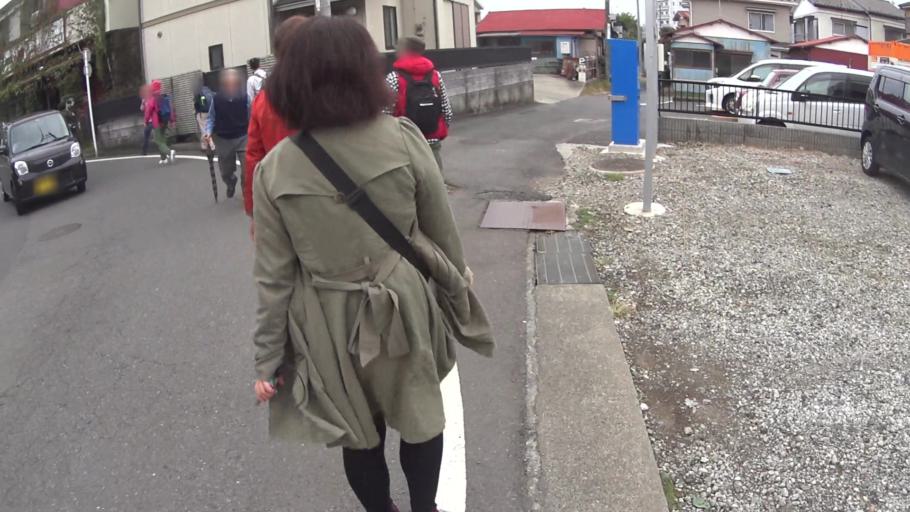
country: JP
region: Kanagawa
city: Hadano
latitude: 35.3777
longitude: 139.2262
